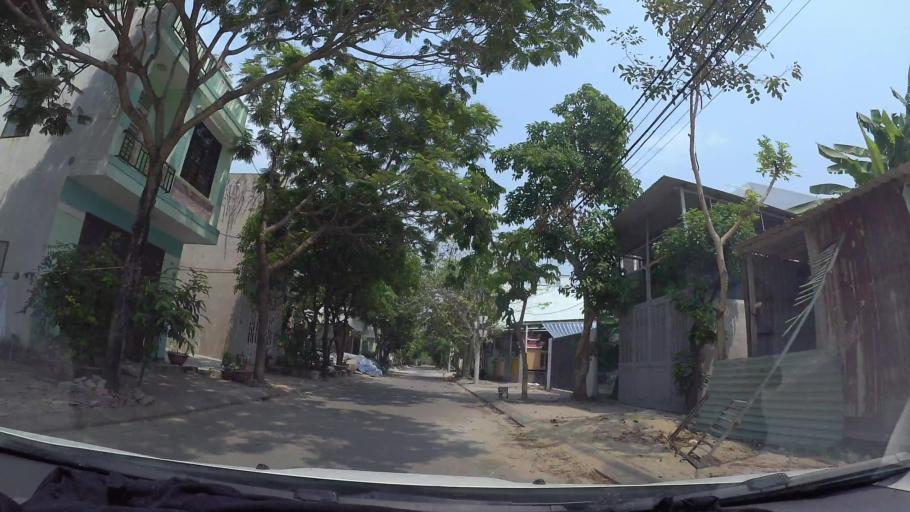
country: VN
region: Da Nang
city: Cam Le
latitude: 16.0051
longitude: 108.2118
